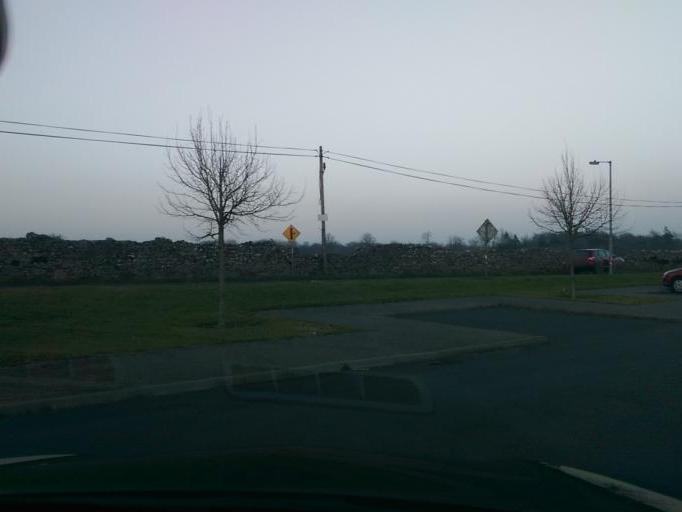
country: IE
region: Connaught
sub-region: County Galway
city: Loughrea
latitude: 53.2289
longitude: -8.6369
